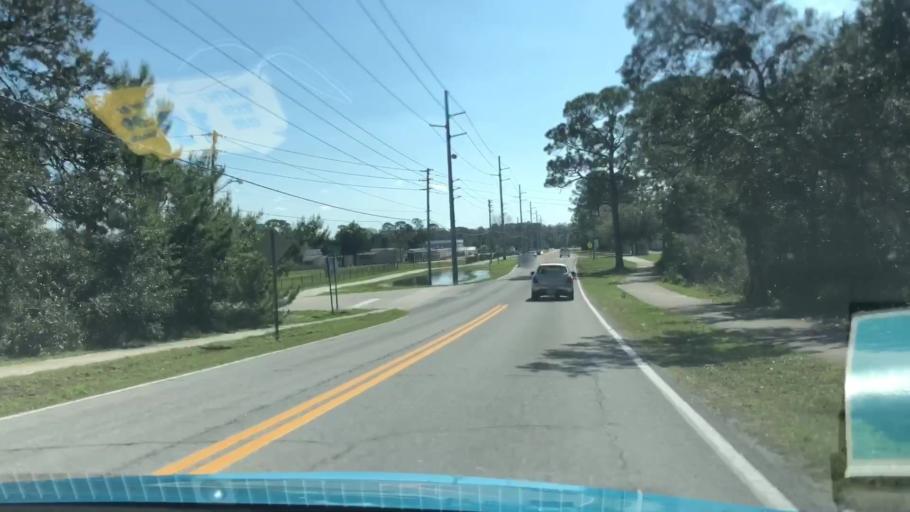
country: US
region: Florida
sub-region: Volusia County
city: Deltona
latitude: 28.8798
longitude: -81.2753
